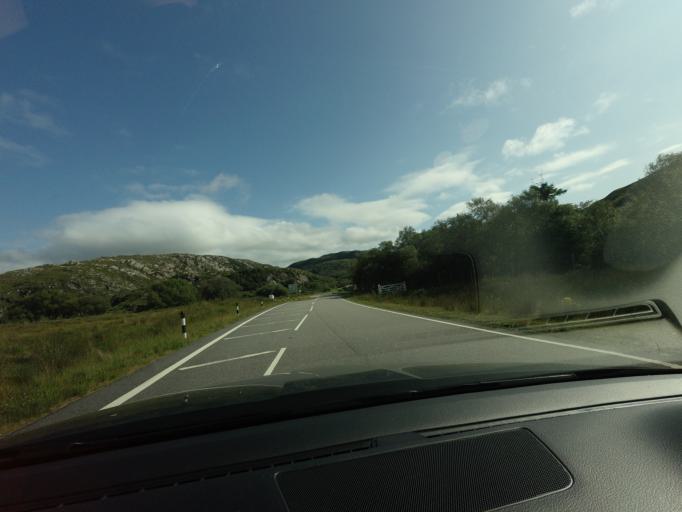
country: GB
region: Scotland
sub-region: Highland
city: Ullapool
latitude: 58.3761
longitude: -5.0170
